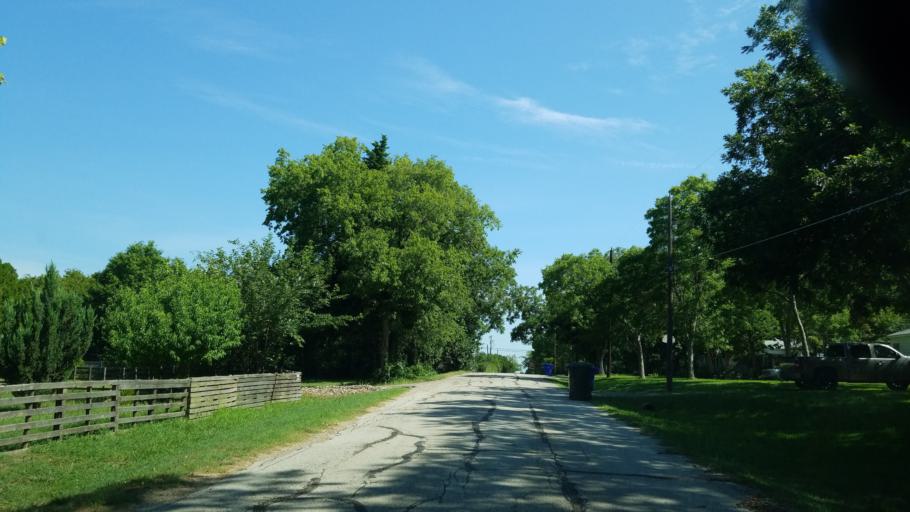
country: US
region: Texas
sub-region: Dallas County
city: Carrollton
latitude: 32.9613
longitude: -96.9121
